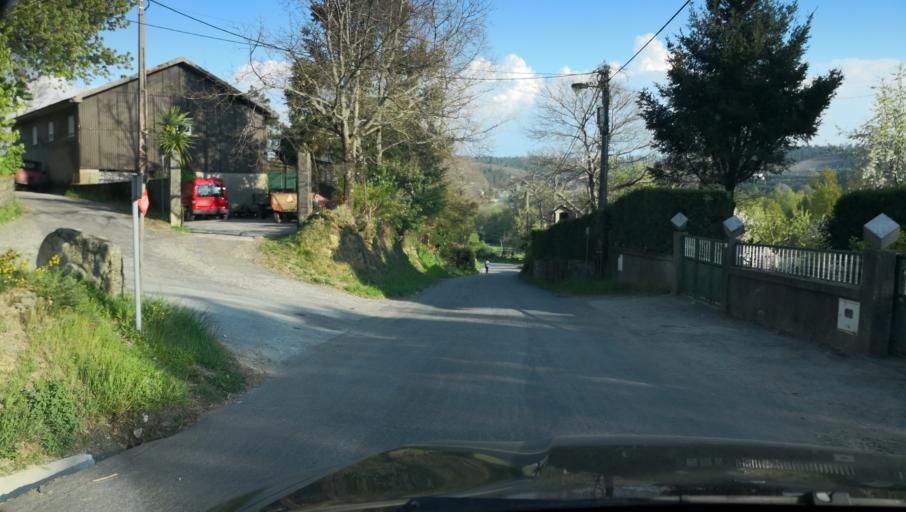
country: PT
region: Vila Real
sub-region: Santa Marta de Penaguiao
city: Santa Marta de Penaguiao
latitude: 41.2887
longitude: -7.8352
